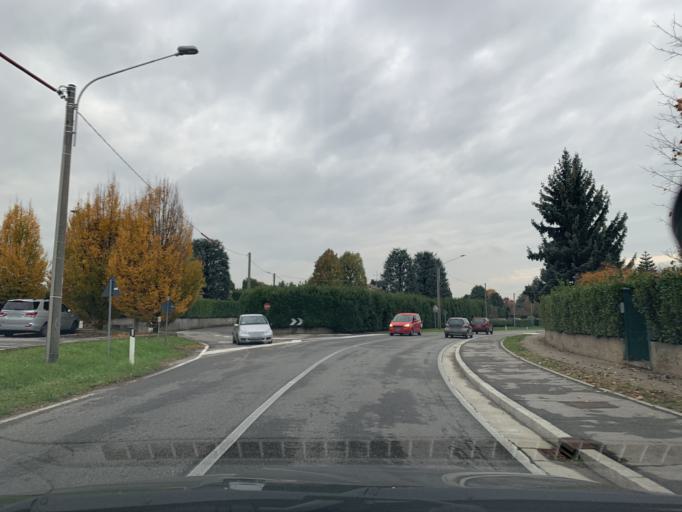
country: IT
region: Lombardy
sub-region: Provincia di Como
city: Bulgorello
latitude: 45.7239
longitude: 9.0586
